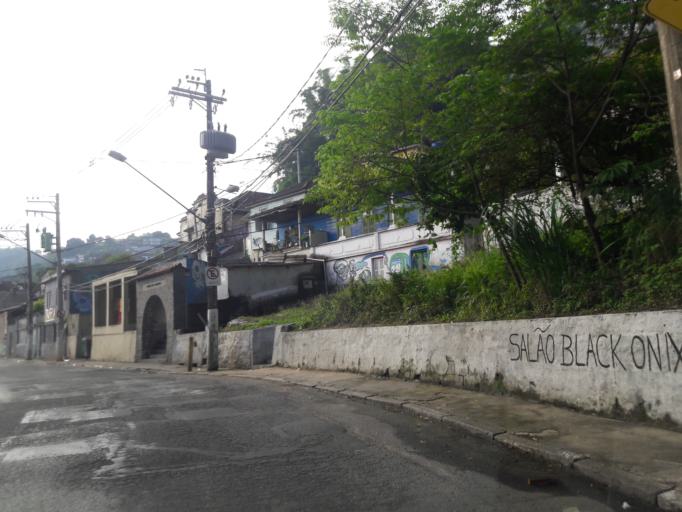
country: BR
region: Sao Paulo
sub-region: Santos
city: Santos
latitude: -23.9327
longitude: -46.3381
